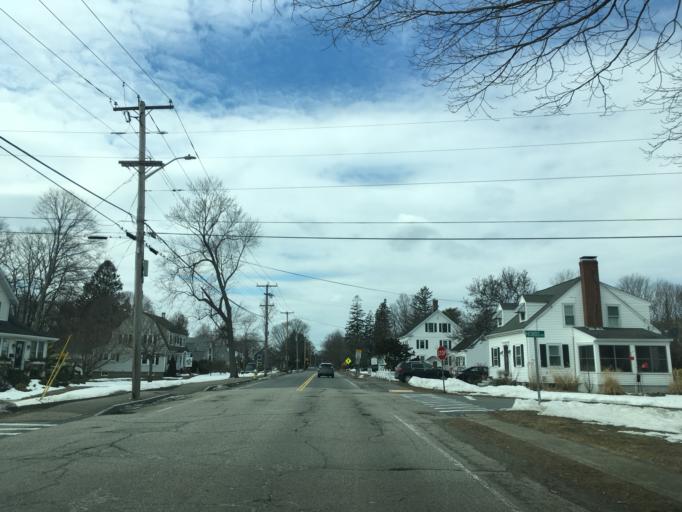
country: US
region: New Hampshire
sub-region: Rockingham County
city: Hampton
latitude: 42.9388
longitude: -70.8266
